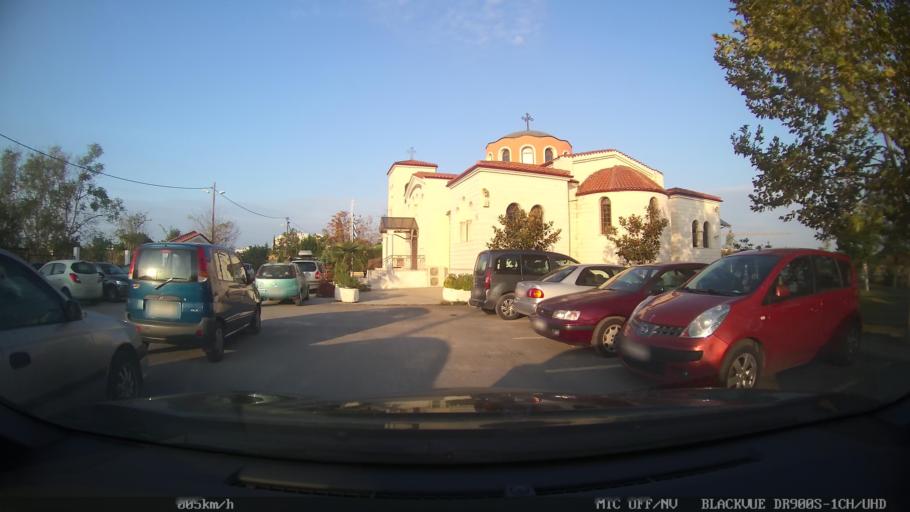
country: GR
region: Central Macedonia
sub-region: Nomos Thessalonikis
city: Pylaia
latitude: 40.5920
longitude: 22.9710
